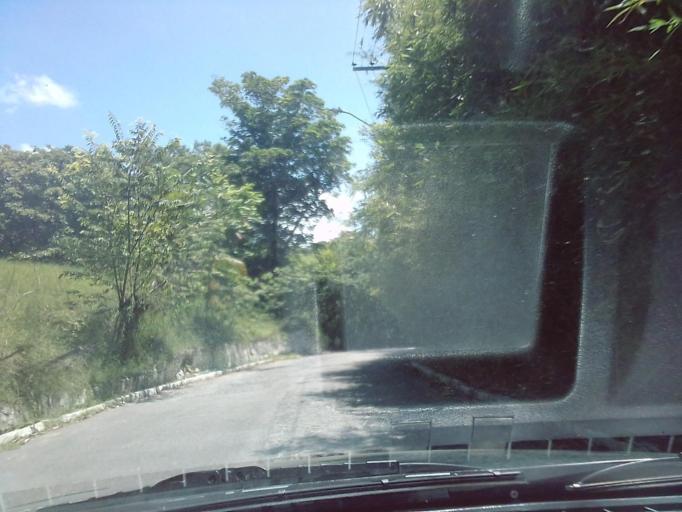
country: BR
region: Pernambuco
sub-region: Igarassu
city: Igarassu
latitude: -7.8458
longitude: -34.8435
